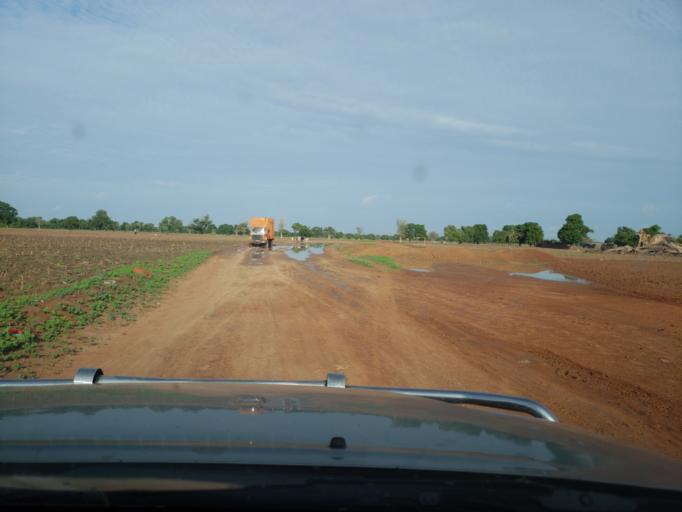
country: ML
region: Sikasso
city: Koutiala
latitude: 12.4219
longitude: -5.6883
